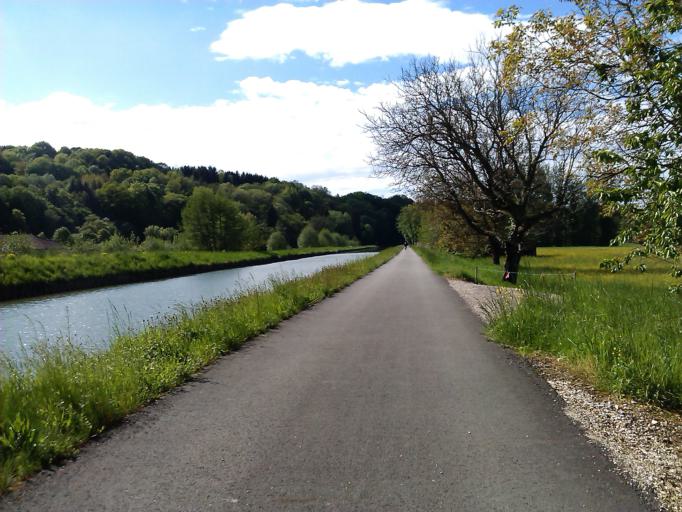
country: FR
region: Franche-Comte
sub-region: Departement du Doubs
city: Montenois
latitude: 47.4306
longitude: 6.6073
